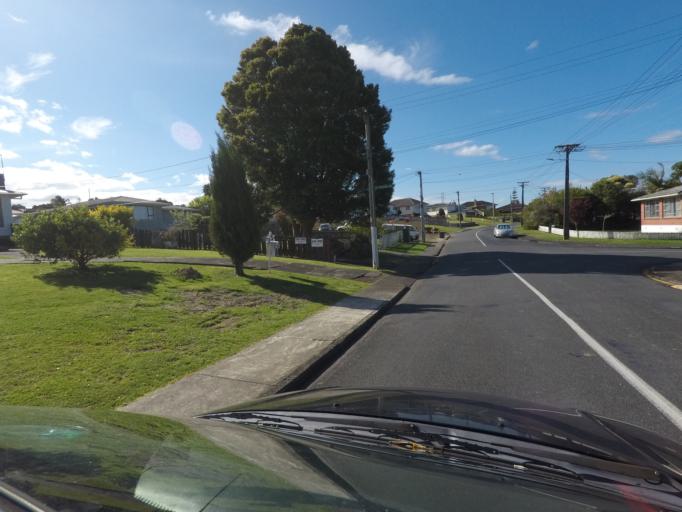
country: NZ
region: Auckland
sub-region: Auckland
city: Rosebank
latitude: -36.8695
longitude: 174.6493
